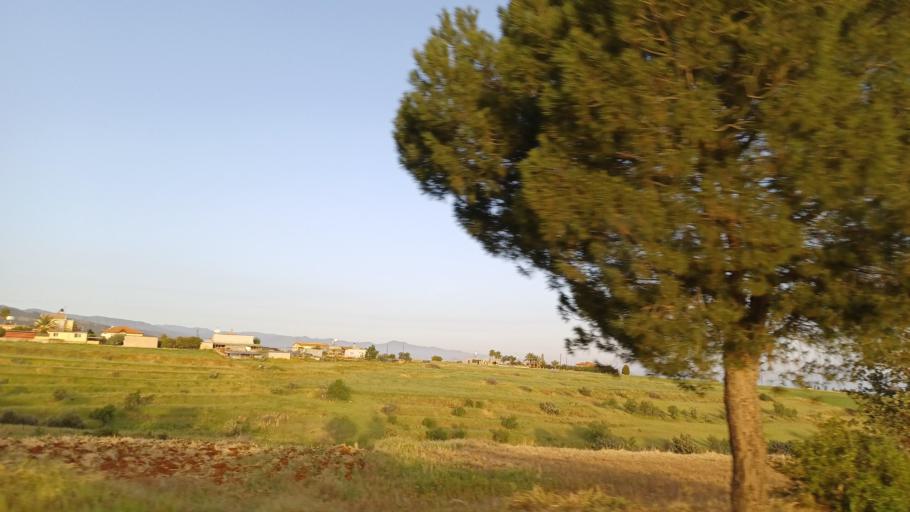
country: CY
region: Lefkosia
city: Astromeritis
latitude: 35.0820
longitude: 33.0160
